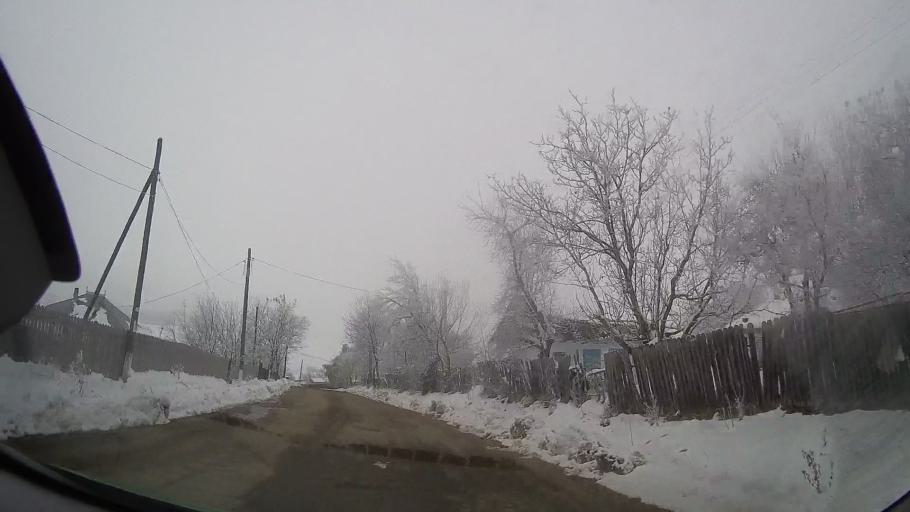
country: RO
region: Iasi
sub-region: Comuna Tansa
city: Tansa
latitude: 46.9144
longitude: 27.2250
